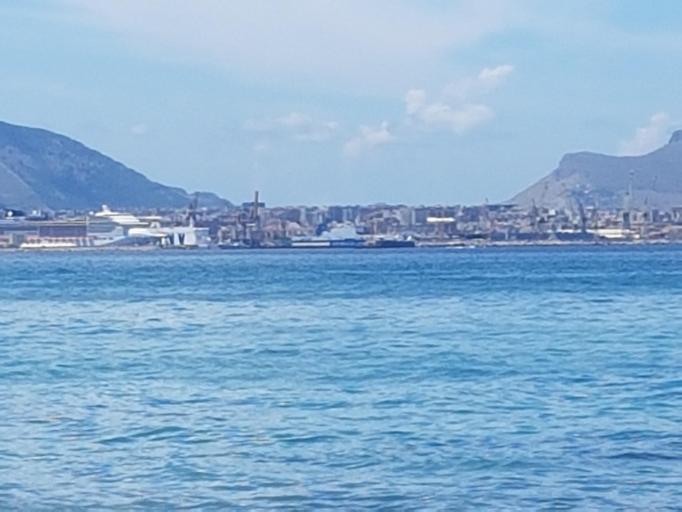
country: IT
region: Sicily
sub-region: Palermo
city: Ciaculli
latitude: 38.0970
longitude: 13.4108
